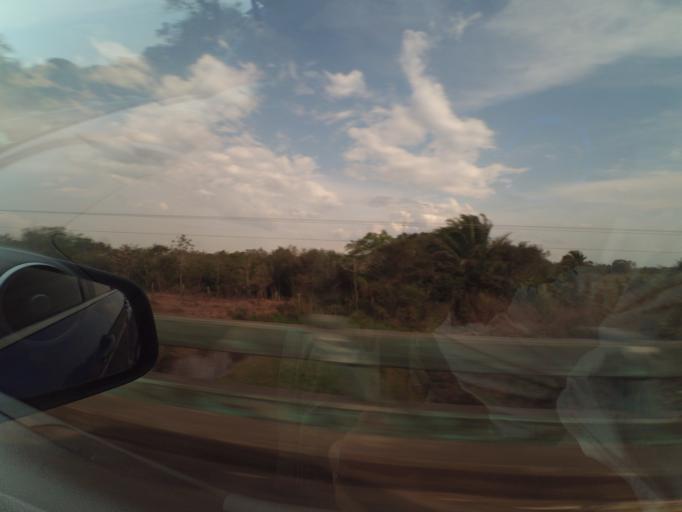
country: BO
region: Santa Cruz
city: Montero
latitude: -17.2629
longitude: -63.0620
